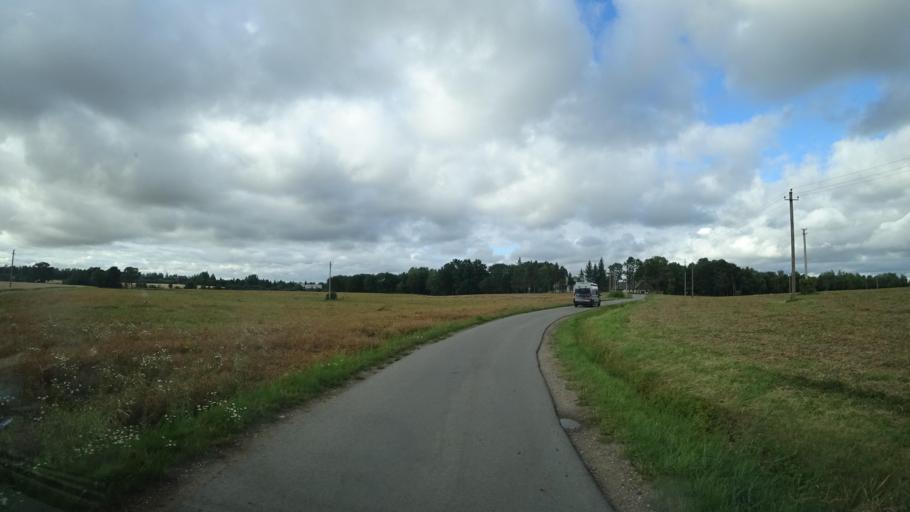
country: LT
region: Marijampoles apskritis
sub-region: Marijampole Municipality
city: Marijampole
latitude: 54.5175
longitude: 23.3273
